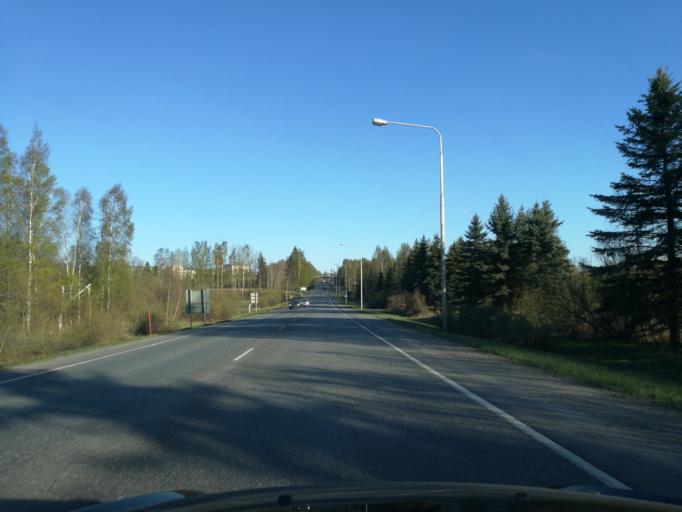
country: FI
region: Uusimaa
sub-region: Helsinki
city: Tuusula
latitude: 60.4017
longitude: 25.0117
